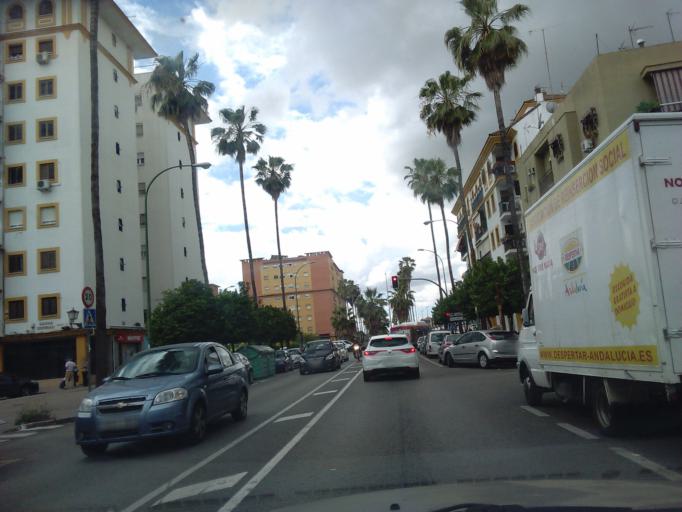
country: ES
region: Andalusia
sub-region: Provincia de Sevilla
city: Sevilla
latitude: 37.3683
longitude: -5.9536
